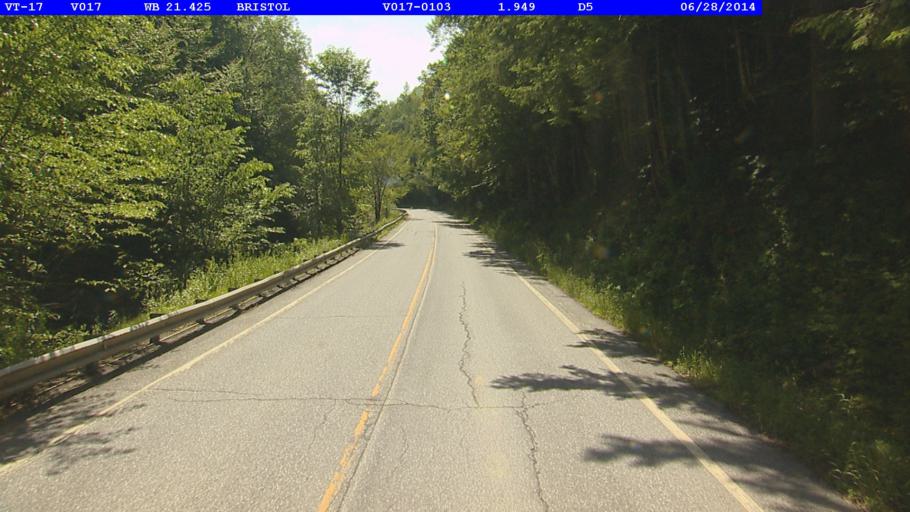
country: US
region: Vermont
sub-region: Addison County
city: Bristol
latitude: 44.1624
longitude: -73.0246
